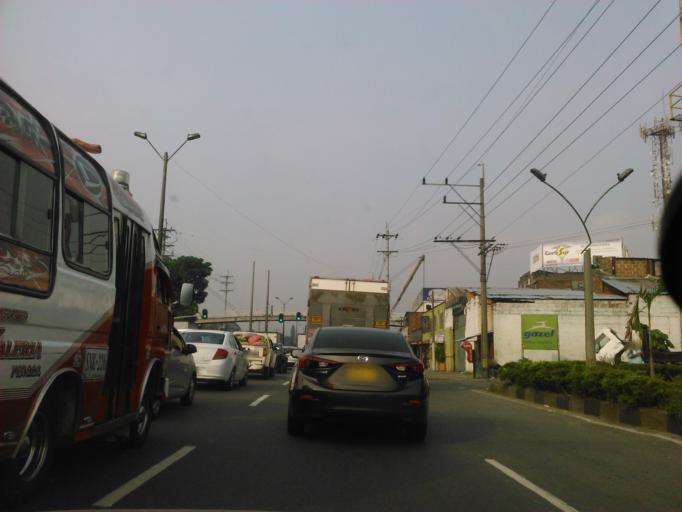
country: CO
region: Antioquia
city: Envigado
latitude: 6.1680
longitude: -75.6070
